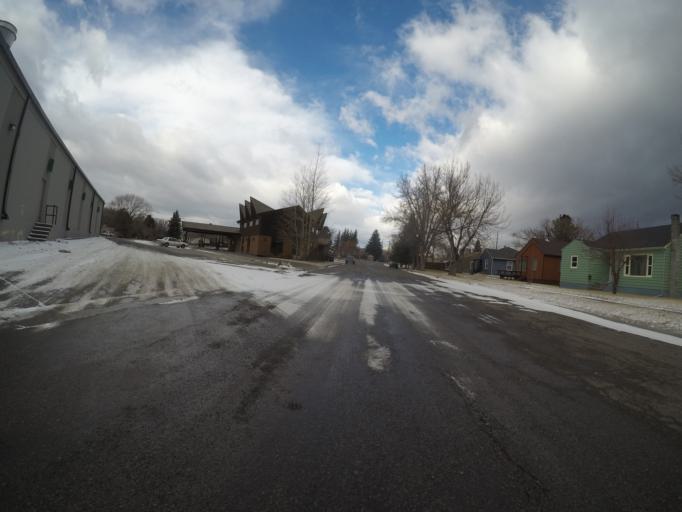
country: US
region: Montana
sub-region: Park County
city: Livingston
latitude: 45.6527
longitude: -110.5705
